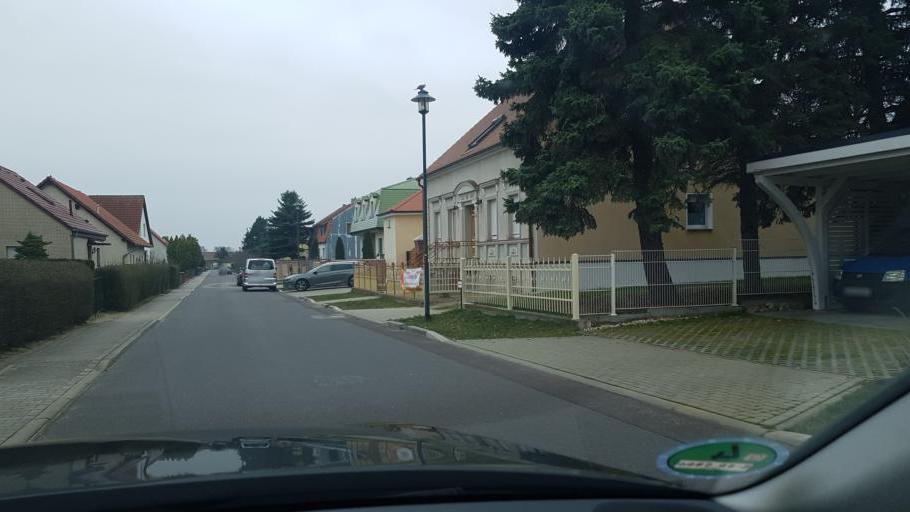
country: DE
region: Brandenburg
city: Mittenwalde
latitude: 52.2893
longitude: 13.5418
